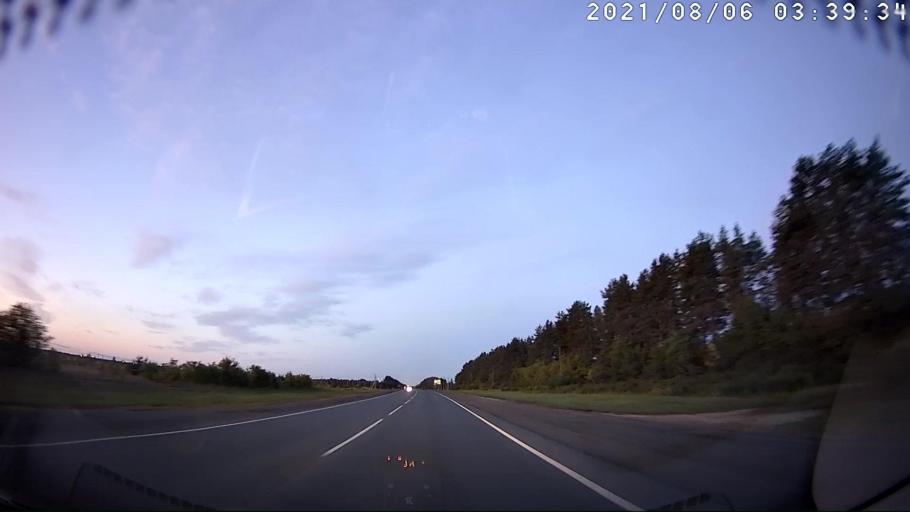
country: RU
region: Mariy-El
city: Pomary
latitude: 55.9592
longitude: 48.3652
